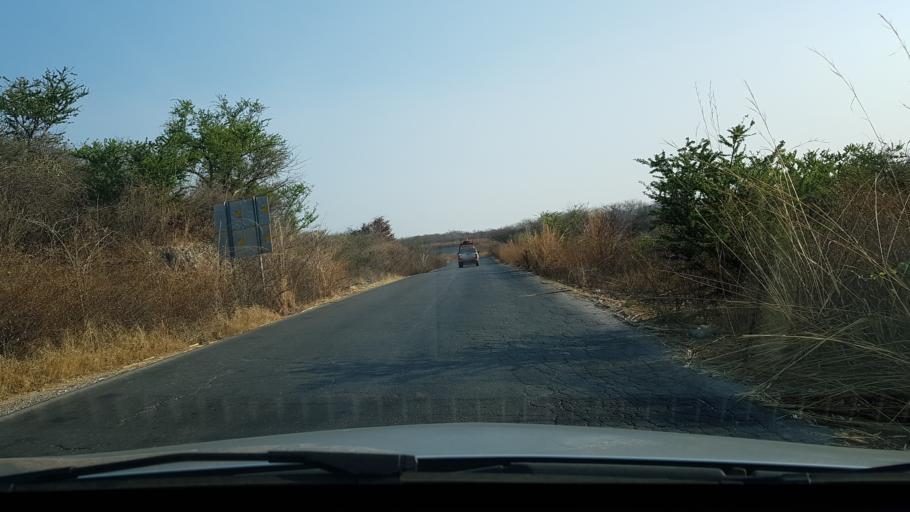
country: MX
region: Morelos
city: Tlaltizapan
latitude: 18.6612
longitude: -99.0462
